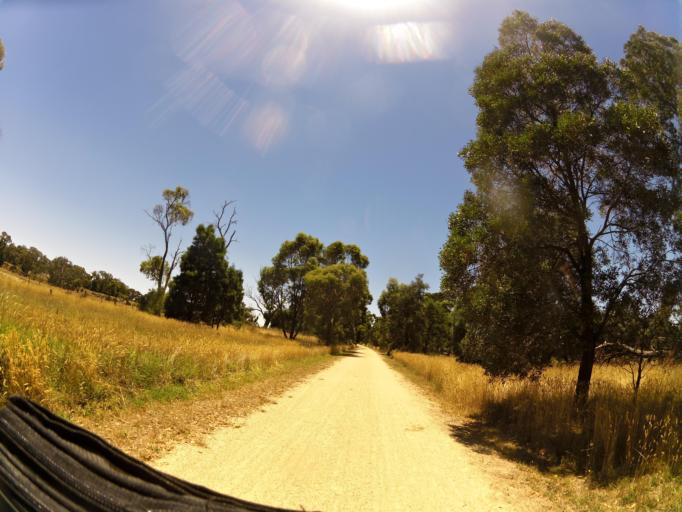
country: AU
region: Victoria
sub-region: Ballarat North
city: Delacombe
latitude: -37.6159
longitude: 143.7106
